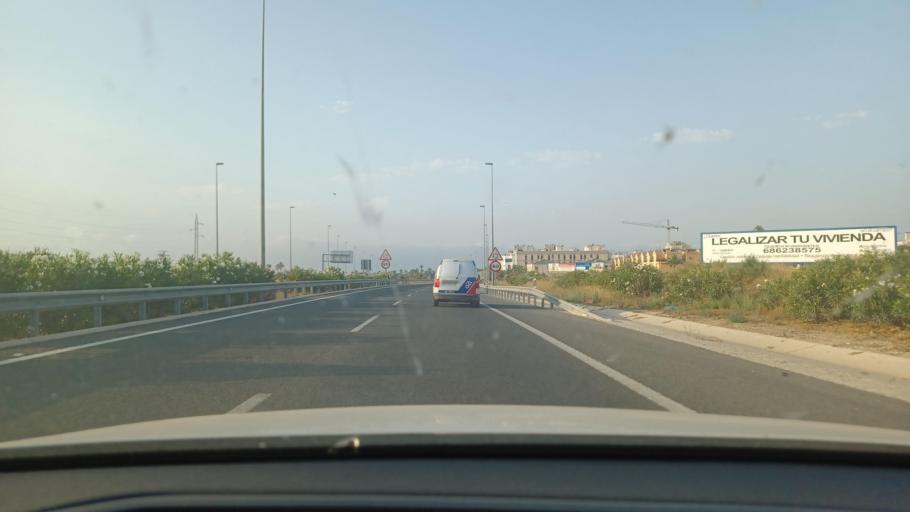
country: ES
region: Valencia
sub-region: Provincia de Alicante
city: Elche
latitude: 38.2681
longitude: -0.6606
